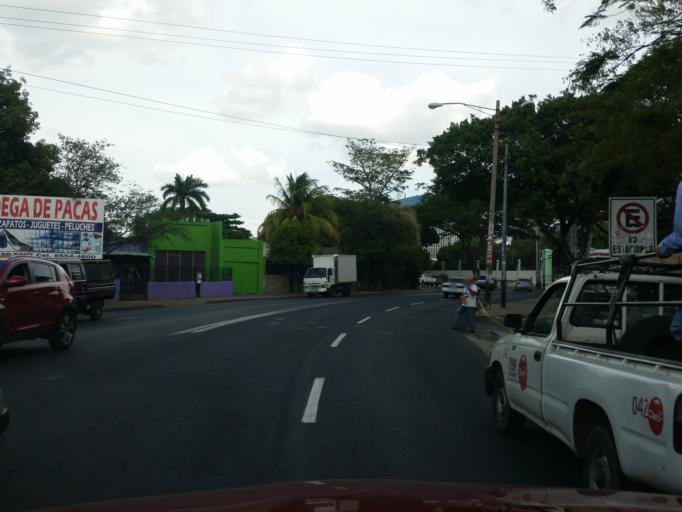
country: NI
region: Managua
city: Managua
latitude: 12.1454
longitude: -86.2709
